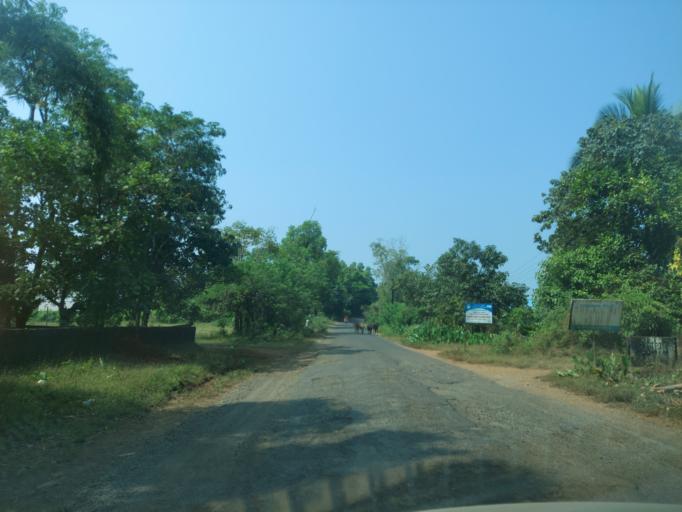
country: IN
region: Maharashtra
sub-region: Sindhudurg
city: Kudal
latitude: 15.9875
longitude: 73.6727
